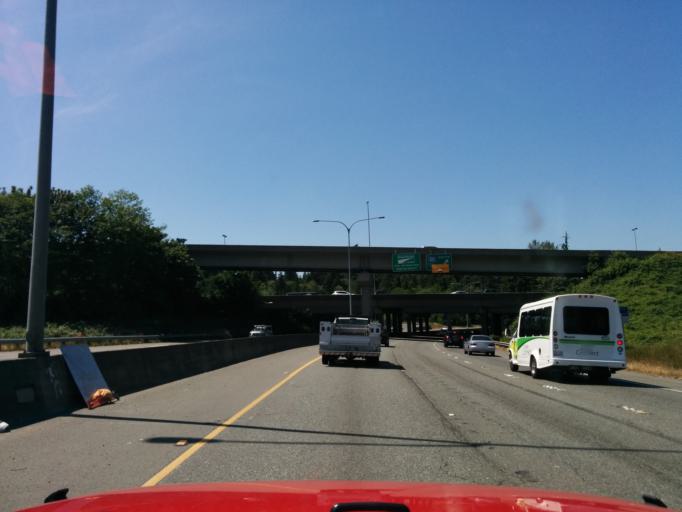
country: US
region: Washington
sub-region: King County
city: Bellevue
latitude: 47.6320
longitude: -122.1862
